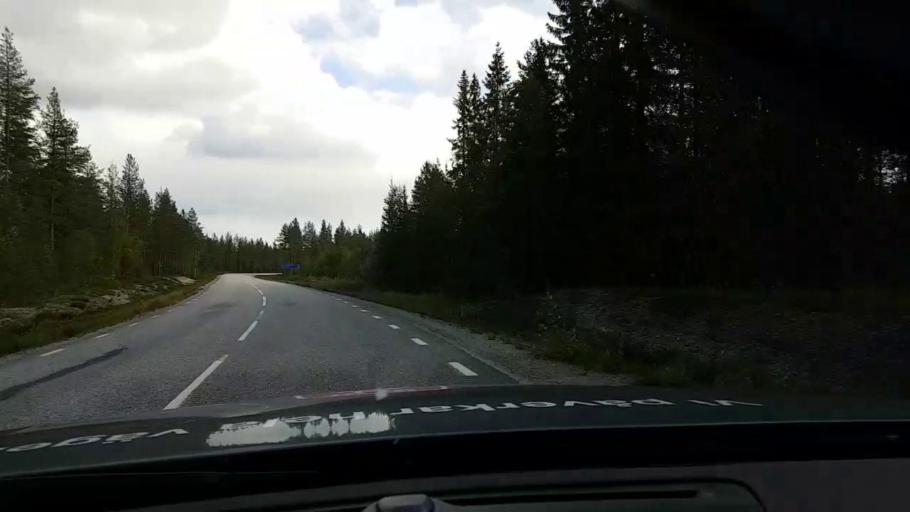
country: SE
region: Vaesternorrland
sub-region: OErnskoeldsviks Kommun
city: Bredbyn
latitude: 63.6858
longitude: 17.7726
